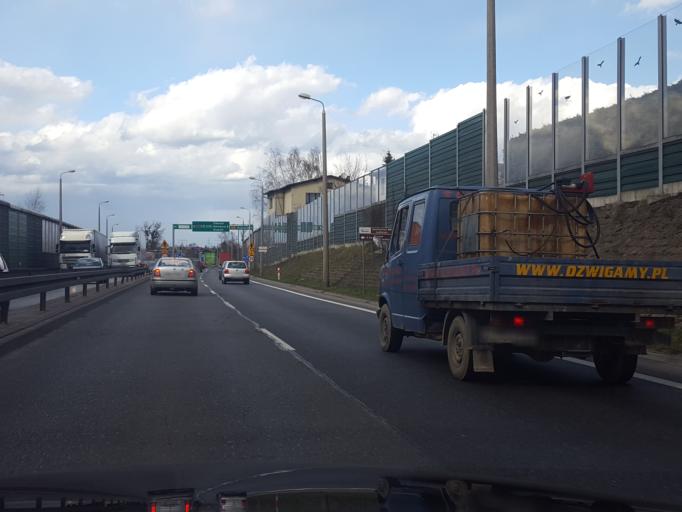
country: PL
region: Silesian Voivodeship
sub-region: Powiat pszczynski
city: Pszczyna
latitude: 49.9733
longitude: 18.9584
